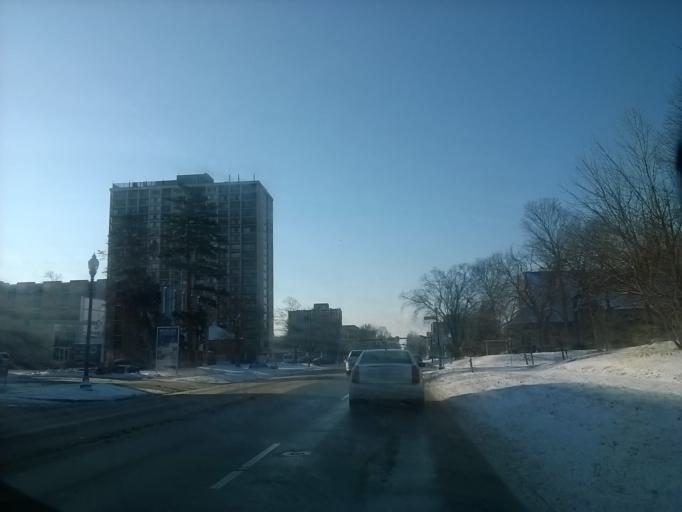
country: US
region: Indiana
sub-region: Marion County
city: Broad Ripple
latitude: 39.8269
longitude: -86.1569
